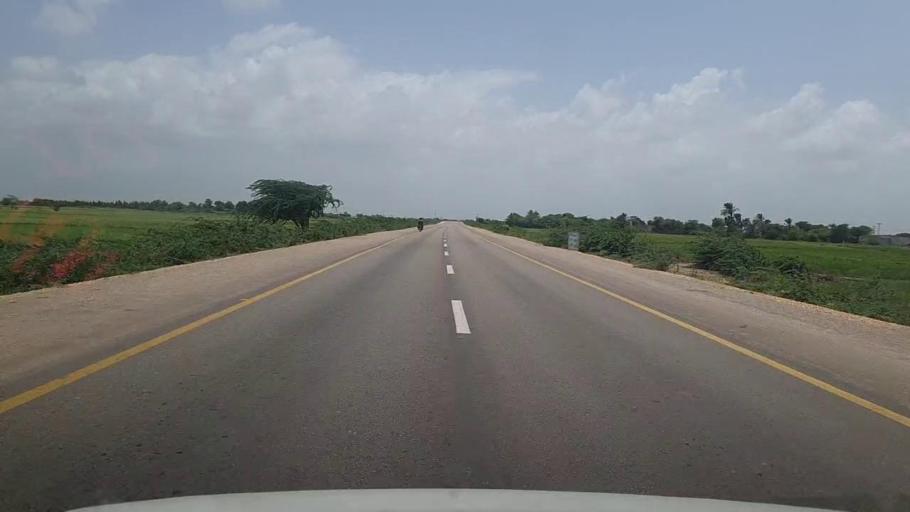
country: PK
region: Sindh
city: Thatta
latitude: 24.7664
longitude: 67.9455
